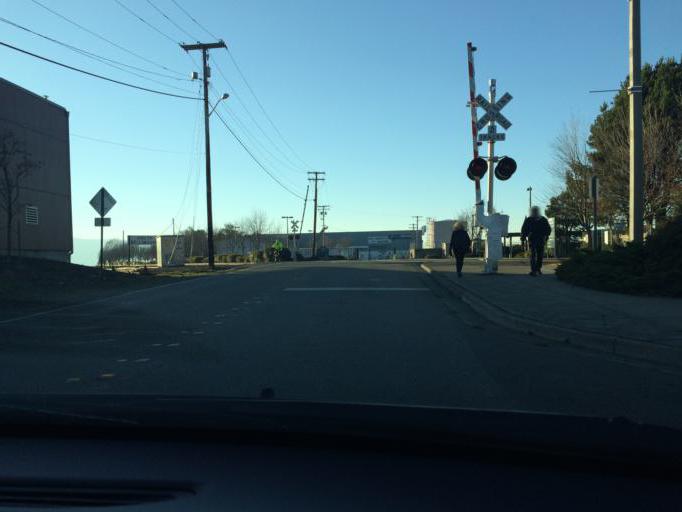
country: US
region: Washington
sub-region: Whatcom County
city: Bellingham
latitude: 48.7201
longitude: -122.5120
